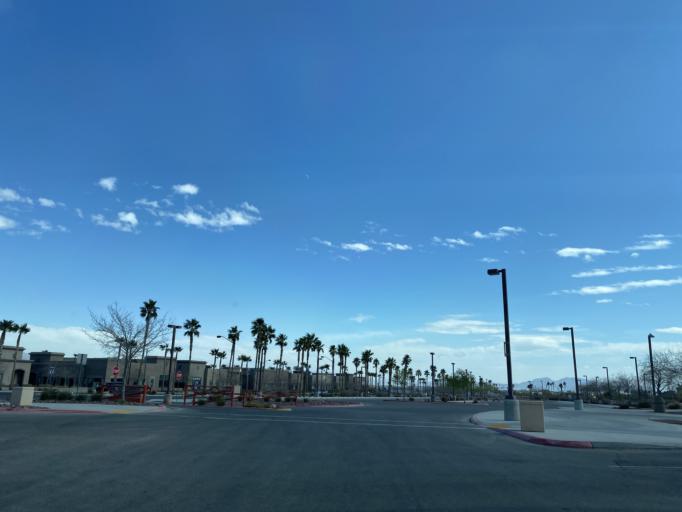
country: US
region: Nevada
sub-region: Clark County
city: Summerlin South
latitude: 36.2734
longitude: -115.2842
